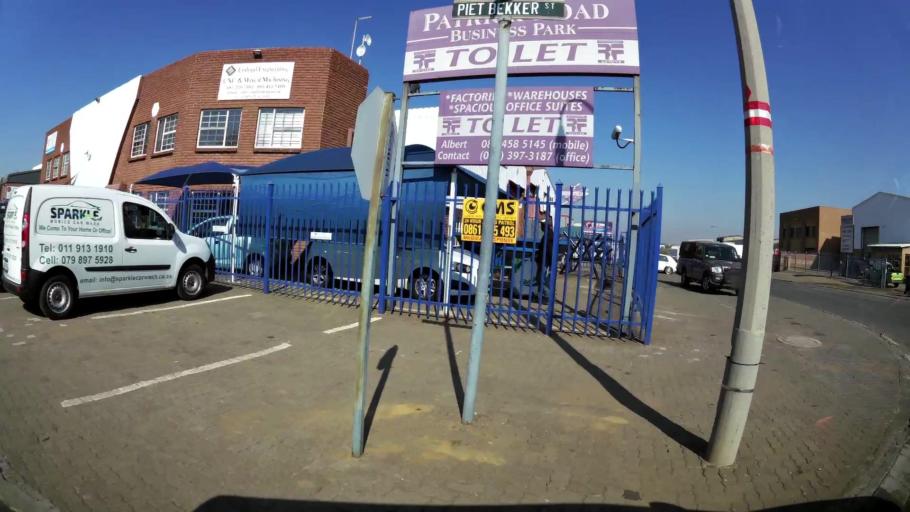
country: ZA
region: Gauteng
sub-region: Ekurhuleni Metropolitan Municipality
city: Boksburg
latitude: -26.1618
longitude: 28.2244
